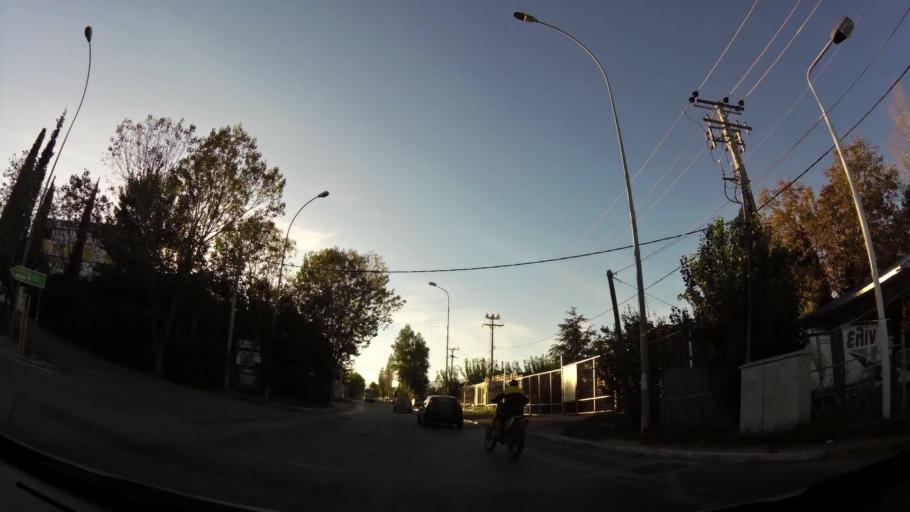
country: GR
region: Attica
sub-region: Nomarchia Anatolikis Attikis
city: Kryoneri
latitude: 38.1405
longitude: 23.8418
